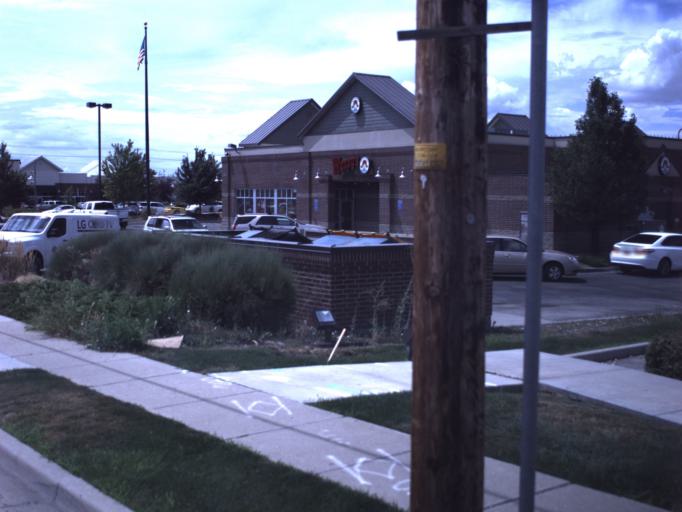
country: US
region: Utah
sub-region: Davis County
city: Syracuse
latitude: 41.0910
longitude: -112.0647
